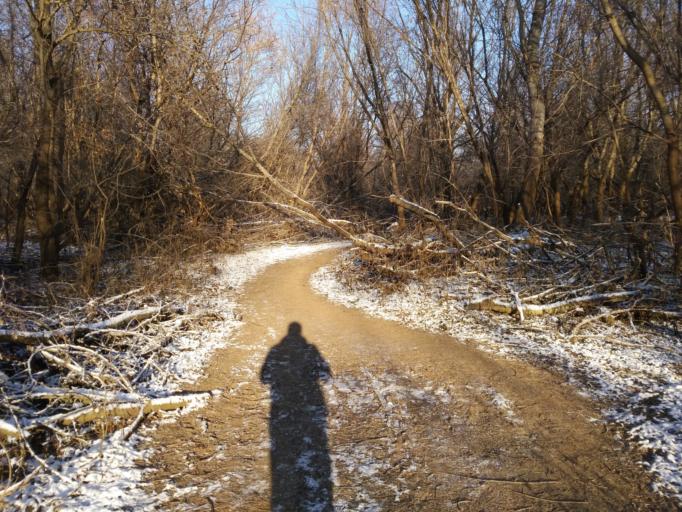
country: RU
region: Kirov
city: Vyatskiye Polyany
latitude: 56.2370
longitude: 51.0790
